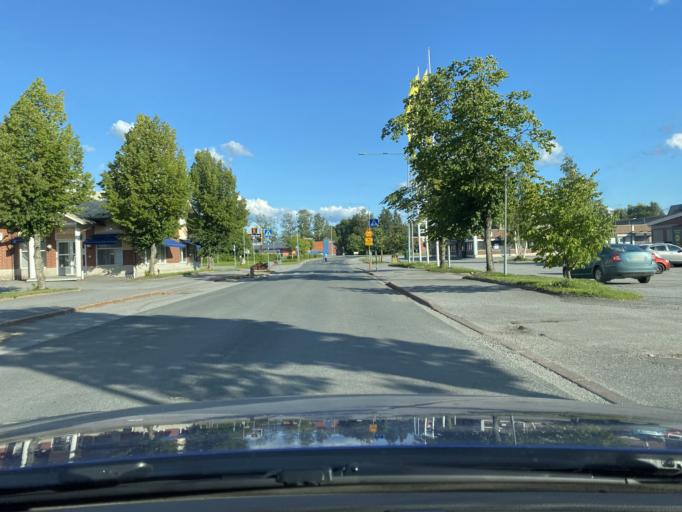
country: FI
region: Ostrobothnia
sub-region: Kyroenmaa
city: Laihia
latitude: 62.9792
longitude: 22.0090
